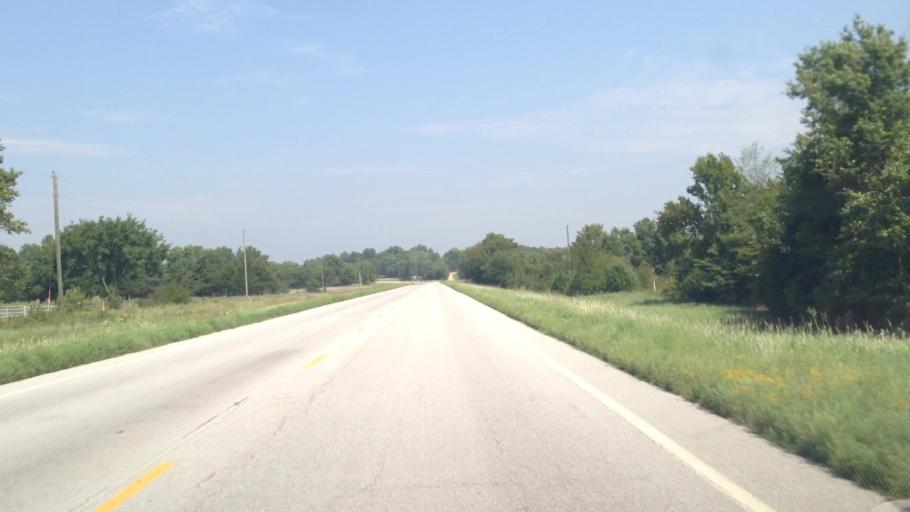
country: US
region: Kansas
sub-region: Labette County
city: Oswego
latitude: 37.1417
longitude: -95.1035
